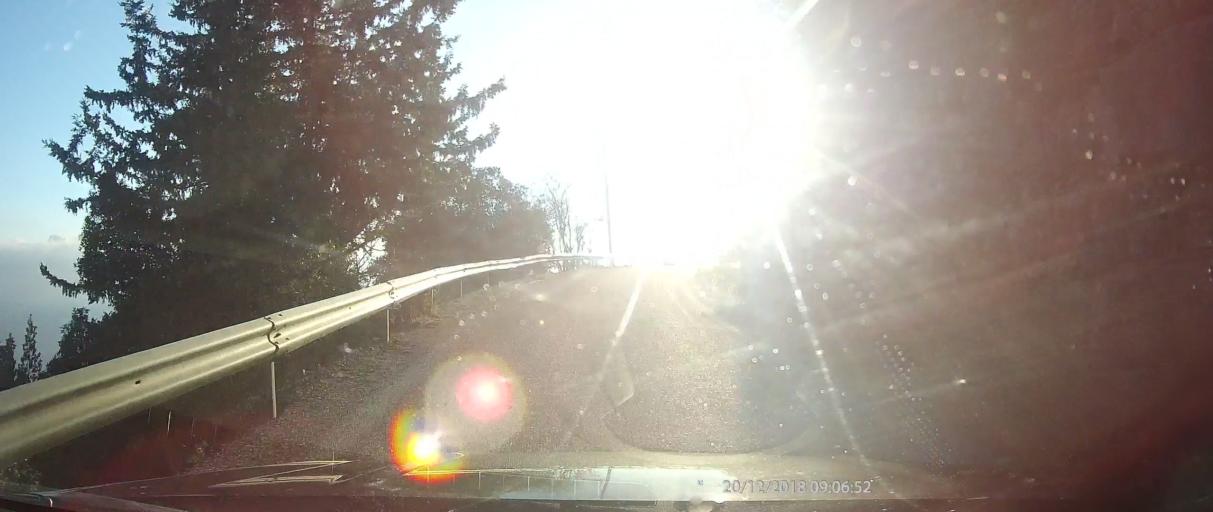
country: GR
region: Peloponnese
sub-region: Nomos Lakonias
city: Sykea
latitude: 36.9303
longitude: 23.0032
